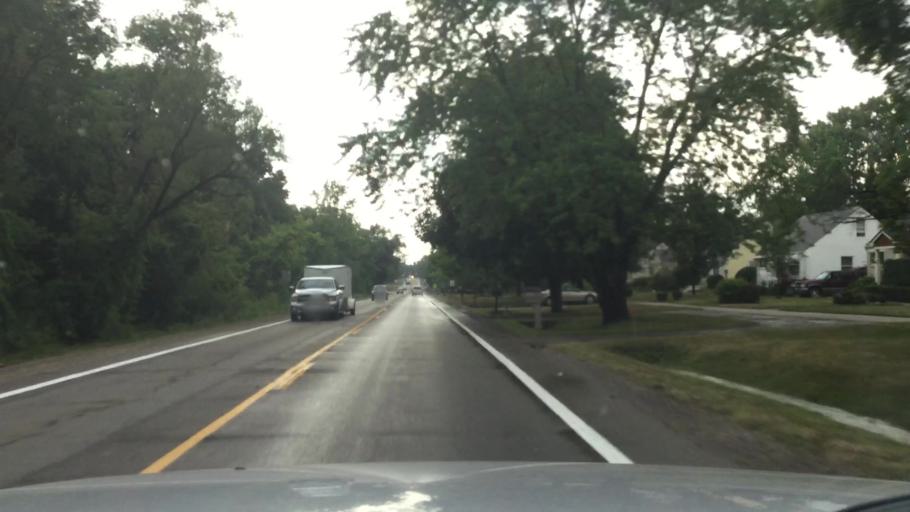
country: US
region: Michigan
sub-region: Oakland County
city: Keego Harbor
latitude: 42.6464
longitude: -83.3460
